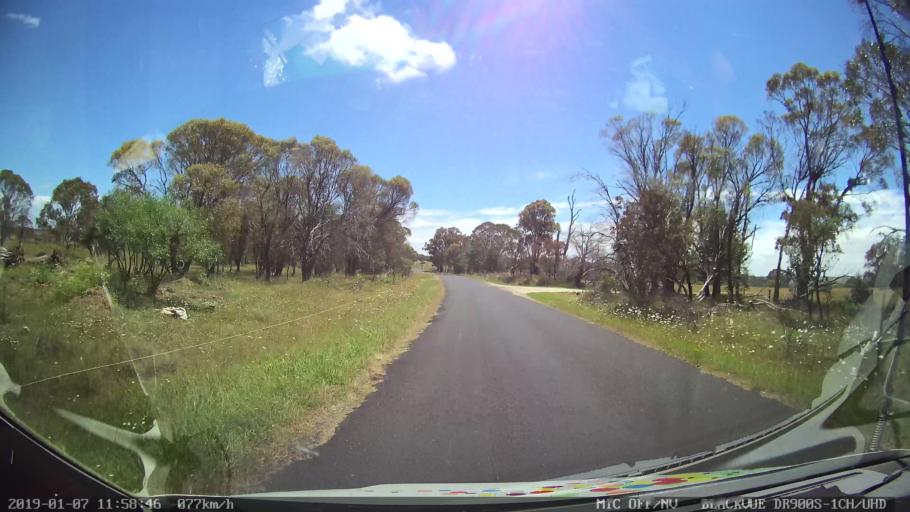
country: AU
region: New South Wales
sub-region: Guyra
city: Guyra
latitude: -30.2496
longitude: 151.6684
